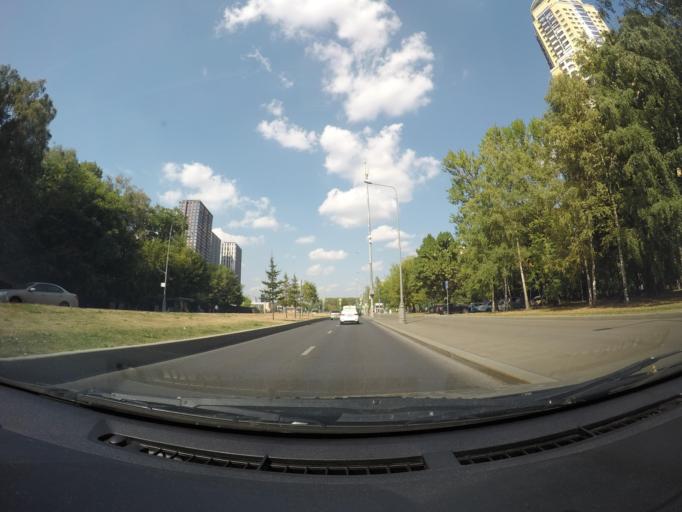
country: RU
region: Moskovskaya
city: Levoberezhnaya
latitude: 55.8759
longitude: 37.4824
